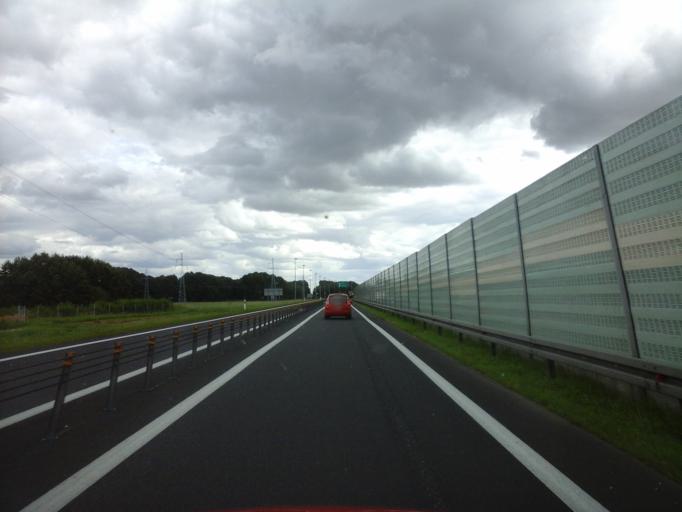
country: PL
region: West Pomeranian Voivodeship
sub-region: Powiat stargardzki
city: Kobylanka
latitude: 53.3555
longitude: 14.9363
